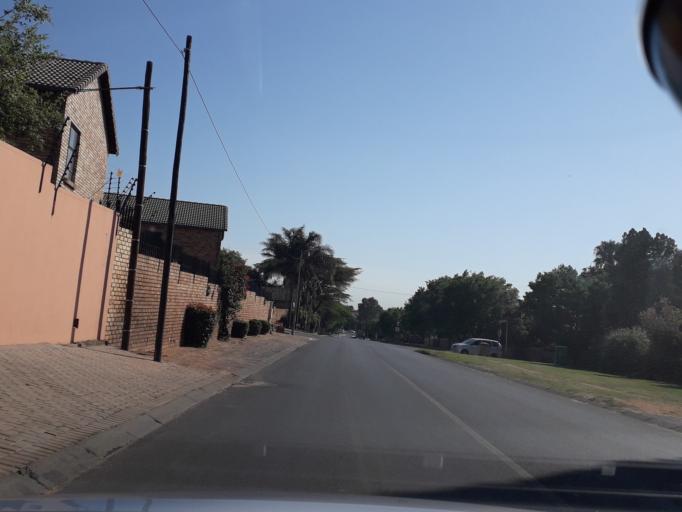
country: ZA
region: Gauteng
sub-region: City of Johannesburg Metropolitan Municipality
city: Roodepoort
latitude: -26.0897
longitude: 27.9320
